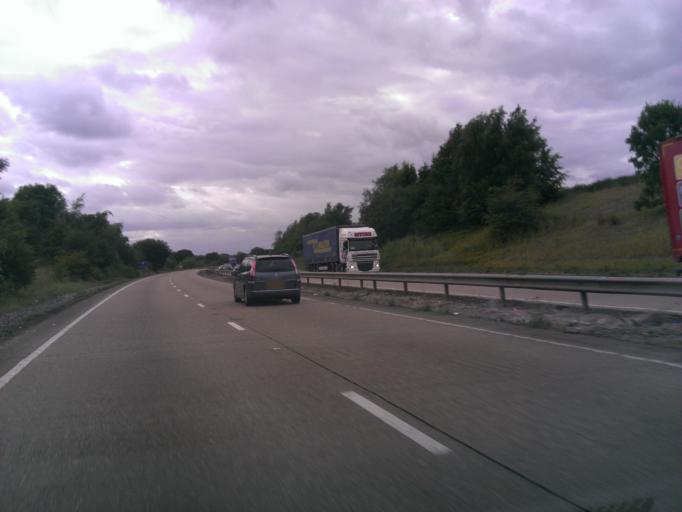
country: GB
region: England
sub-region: Essex
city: Alresford
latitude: 51.8863
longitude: 1.0226
